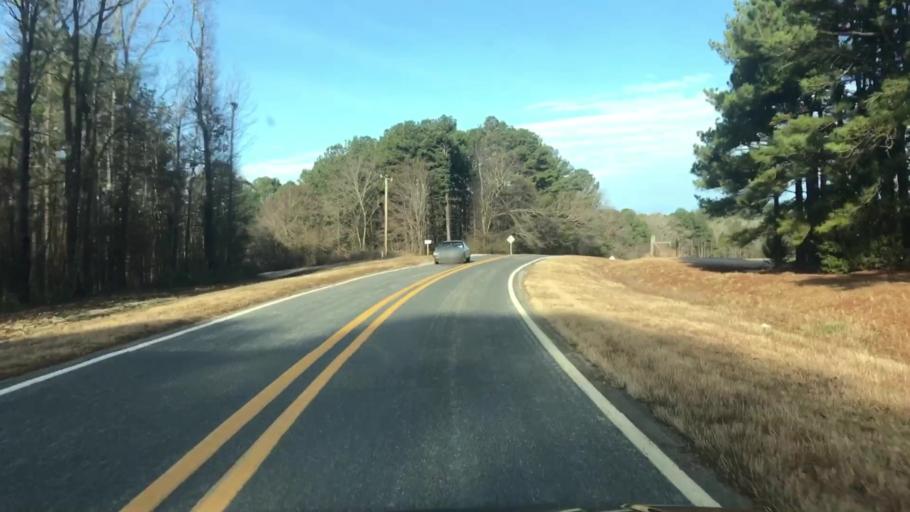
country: US
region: Arkansas
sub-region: Garland County
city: Rockwell
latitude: 34.4787
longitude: -93.2699
